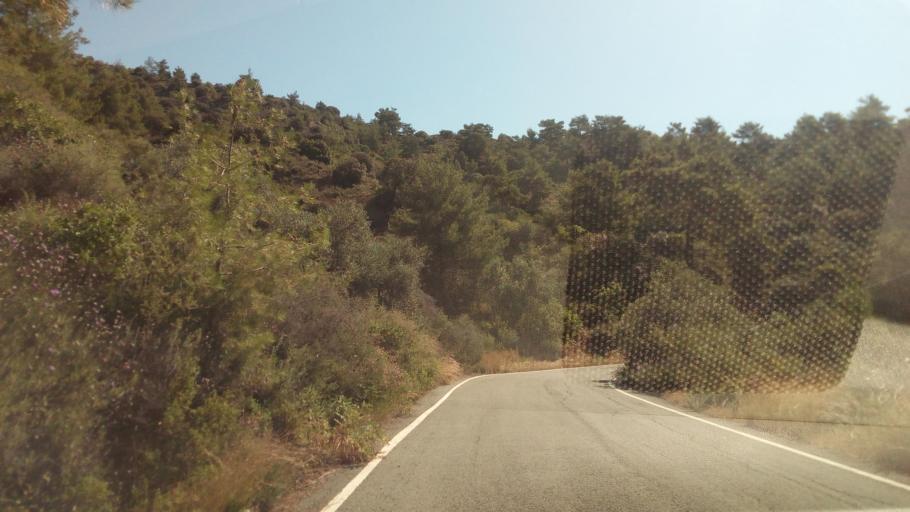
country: CY
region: Lefkosia
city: Lythrodontas
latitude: 34.8887
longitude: 33.2221
